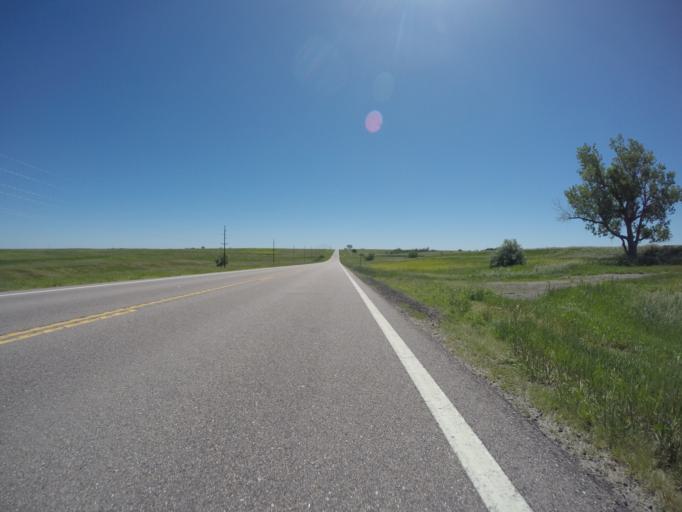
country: US
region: Kansas
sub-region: Norton County
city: Norton
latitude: 39.8284
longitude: -99.6691
